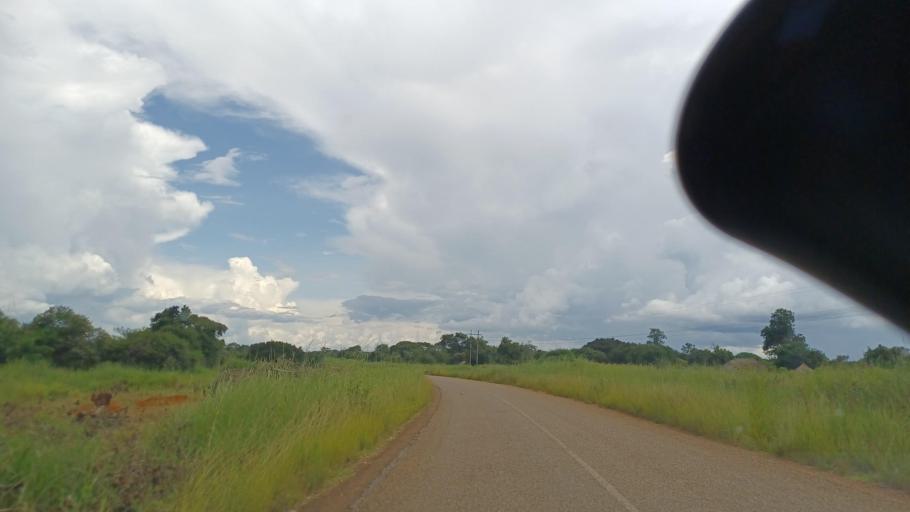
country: ZM
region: North-Western
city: Kasempa
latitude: -13.1225
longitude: 25.8706
